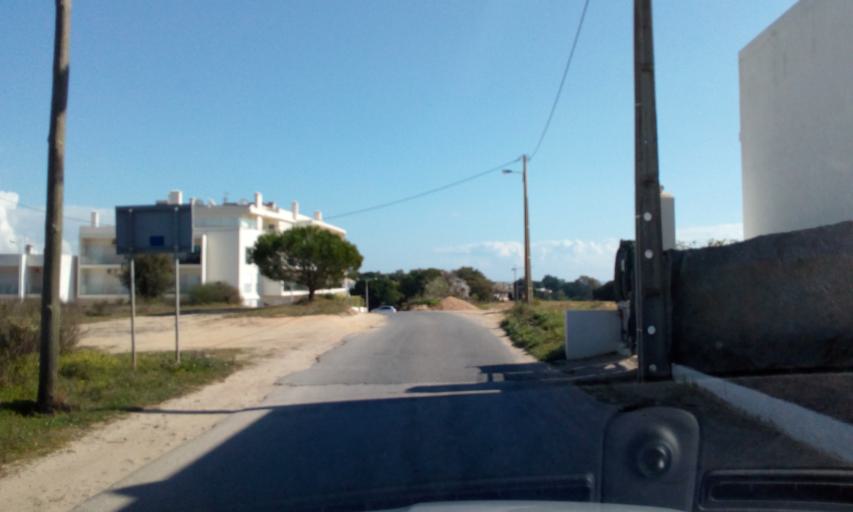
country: PT
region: Faro
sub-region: Albufeira
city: Albufeira
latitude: 37.0962
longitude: -8.2038
